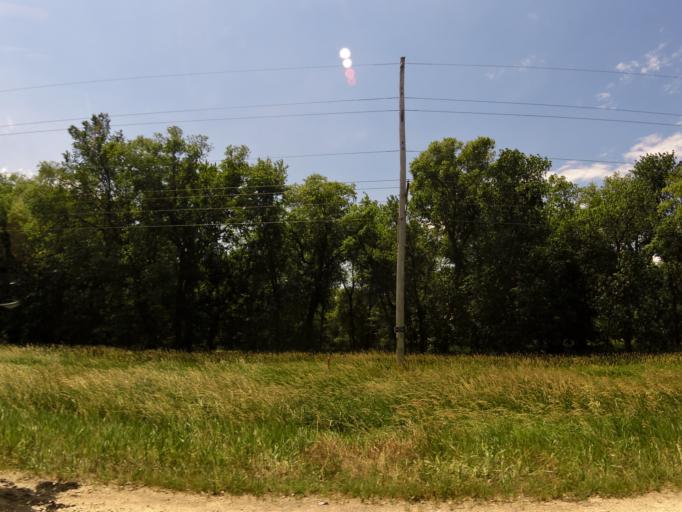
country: US
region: Iowa
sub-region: Bremer County
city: Tripoli
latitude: 42.7148
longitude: -92.1757
